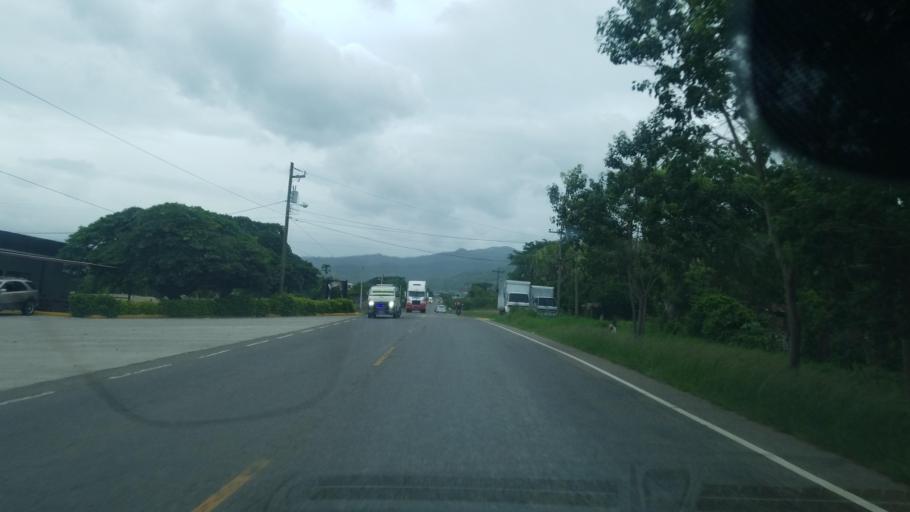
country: HN
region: Ocotepeque
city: Santa Lucia
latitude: 14.4212
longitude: -89.1879
